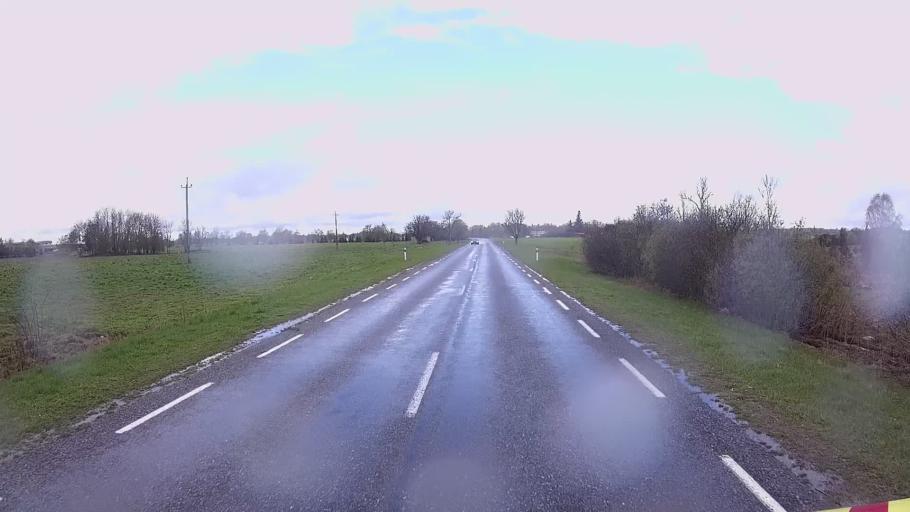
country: EE
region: Hiiumaa
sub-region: Kaerdla linn
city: Kardla
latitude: 58.8337
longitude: 22.8116
